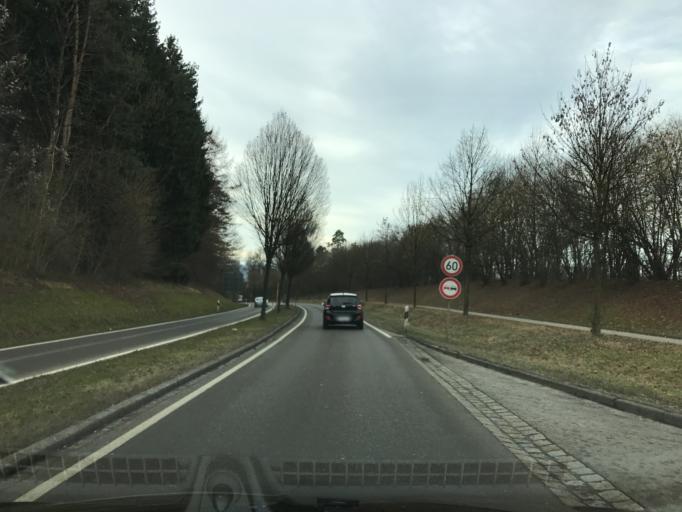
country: DE
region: Bavaria
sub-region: Swabia
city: Weissensberg
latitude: 47.5748
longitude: 9.7080
